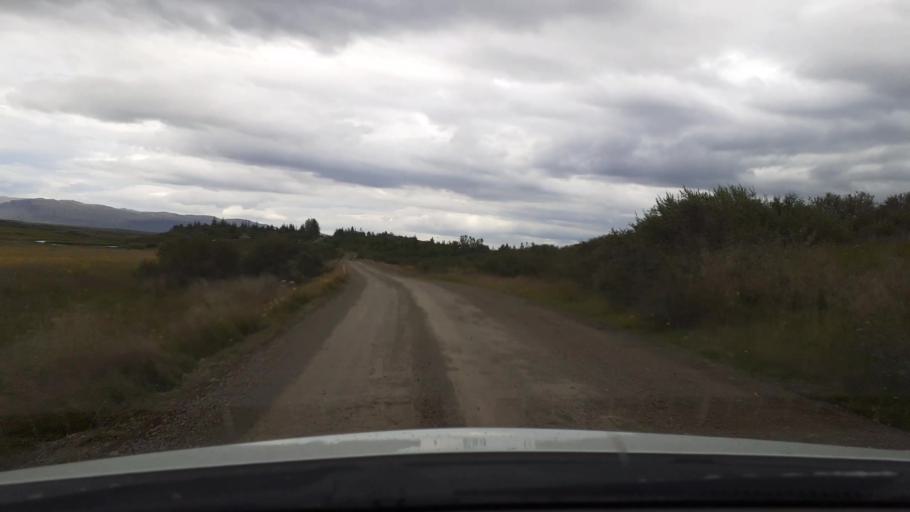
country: IS
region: West
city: Borgarnes
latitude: 64.6118
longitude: -21.9527
